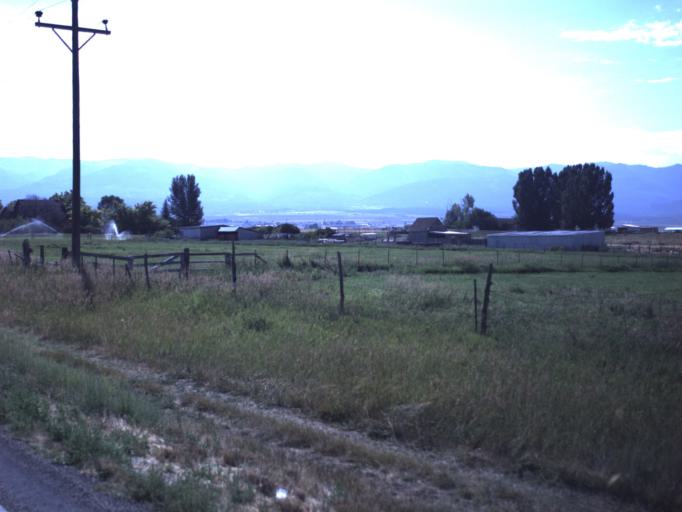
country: US
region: Utah
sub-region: Sanpete County
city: Mount Pleasant
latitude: 39.5467
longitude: -111.5068
